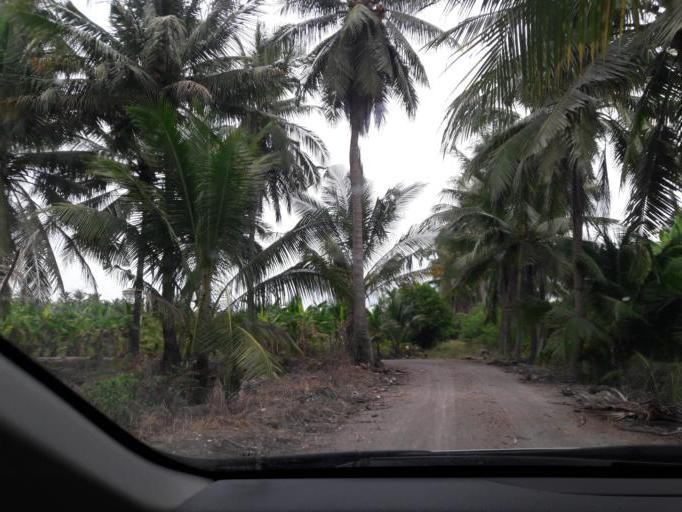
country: TH
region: Samut Sakhon
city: Ban Phaeo
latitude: 13.6042
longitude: 100.0257
